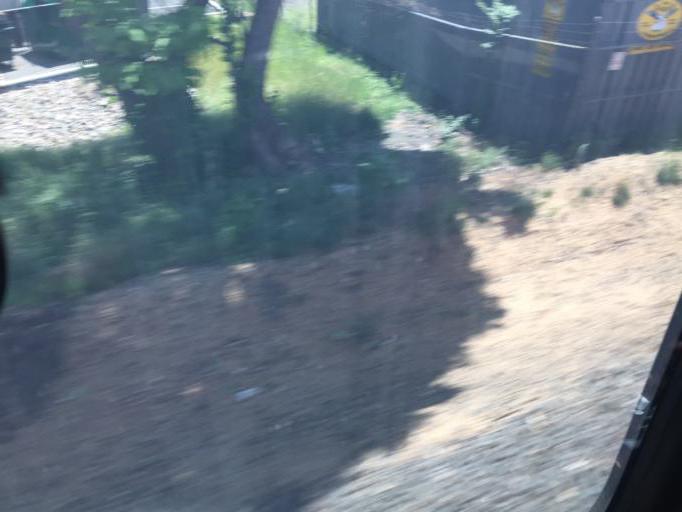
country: US
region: Connecticut
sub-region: New Haven County
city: Wallingford
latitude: 41.4710
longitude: -72.8175
